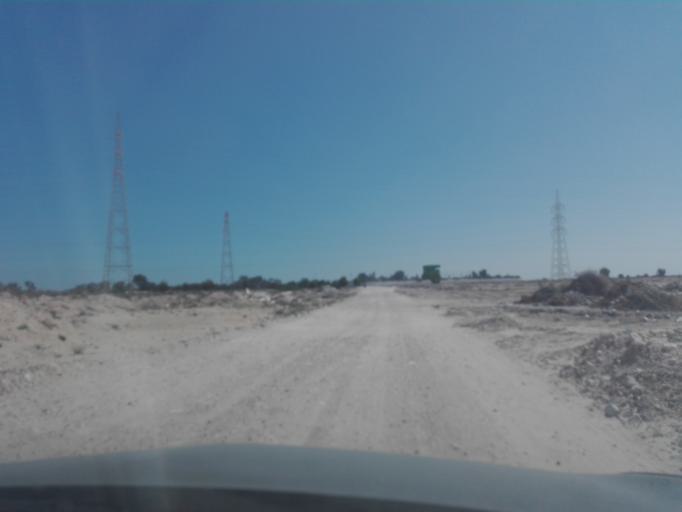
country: TN
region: Qabis
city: Gabes
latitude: 33.8740
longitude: 10.0299
